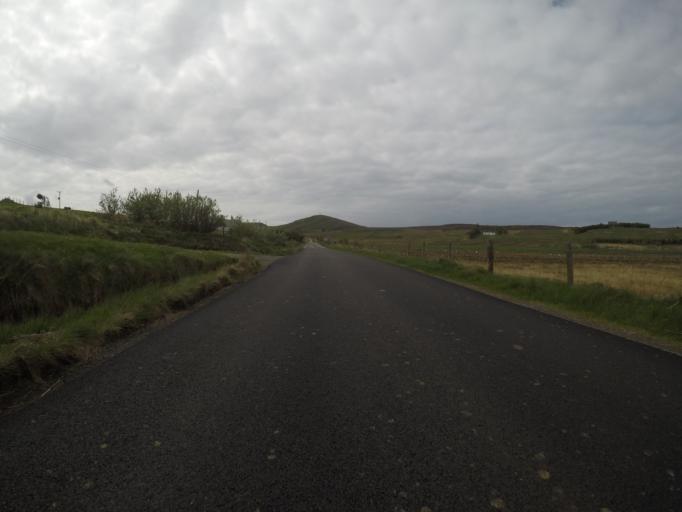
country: GB
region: Scotland
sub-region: Highland
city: Portree
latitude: 57.6846
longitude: -6.3135
